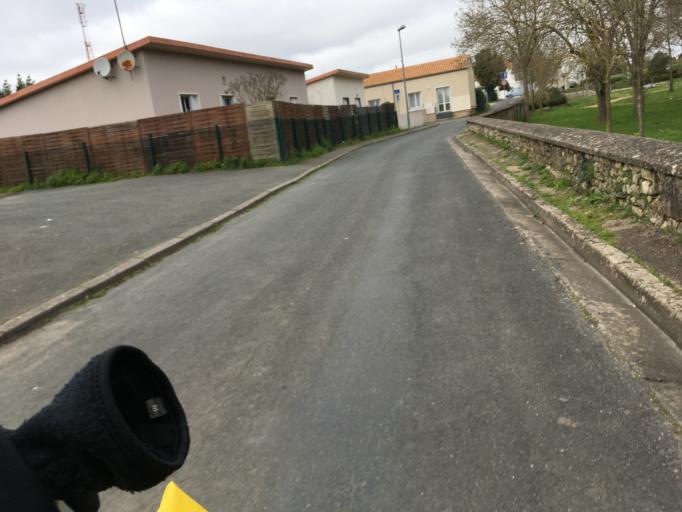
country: FR
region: Poitou-Charentes
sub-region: Departement de la Charente-Maritime
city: La Rochelle
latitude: 46.1778
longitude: -1.1452
